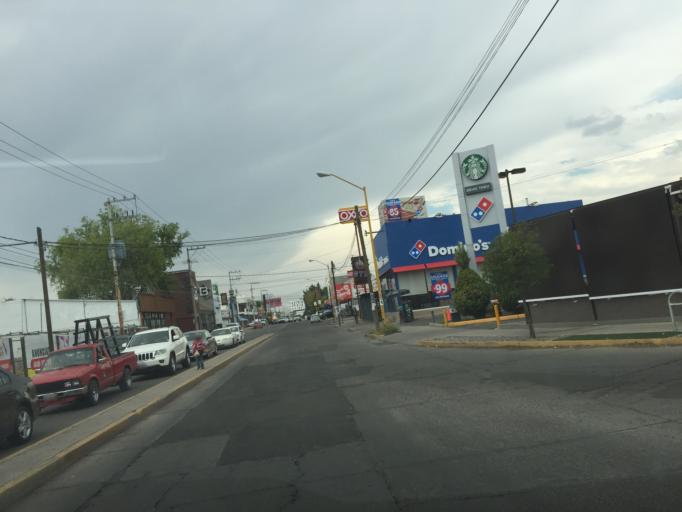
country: MX
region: Aguascalientes
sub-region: Jesus Maria
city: El Llano
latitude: 21.9248
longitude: -102.3048
